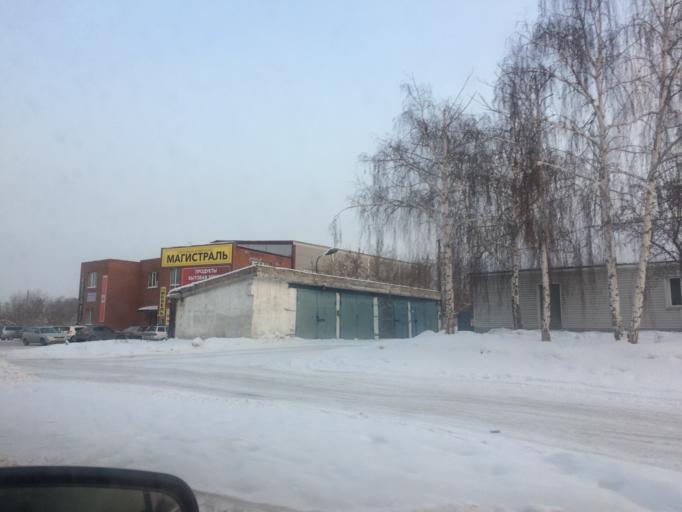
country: RU
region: Chelyabinsk
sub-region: Gorod Magnitogorsk
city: Magnitogorsk
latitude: 53.4657
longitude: 59.0721
